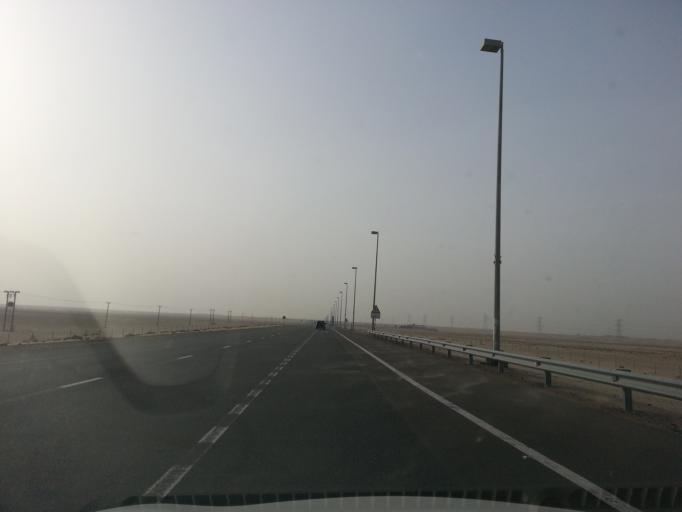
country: AE
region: Dubai
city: Dubai
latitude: 24.7954
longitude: 55.0749
